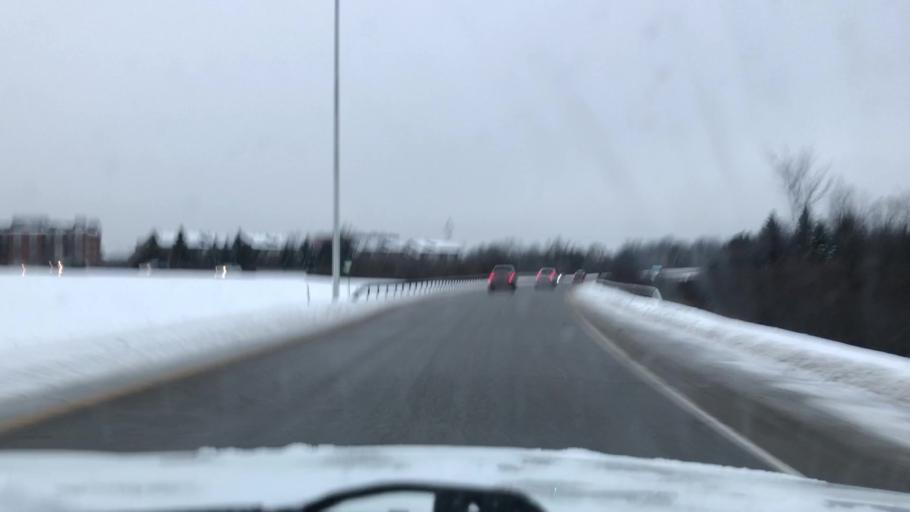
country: CA
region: Ontario
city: Ottawa
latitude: 45.4241
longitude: -75.6224
